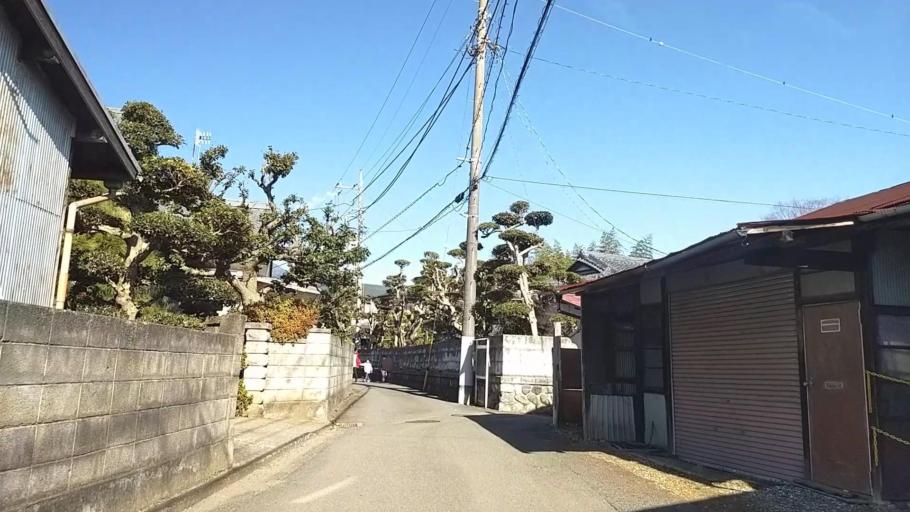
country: JP
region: Kanagawa
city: Hadano
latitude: 35.3749
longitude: 139.2311
